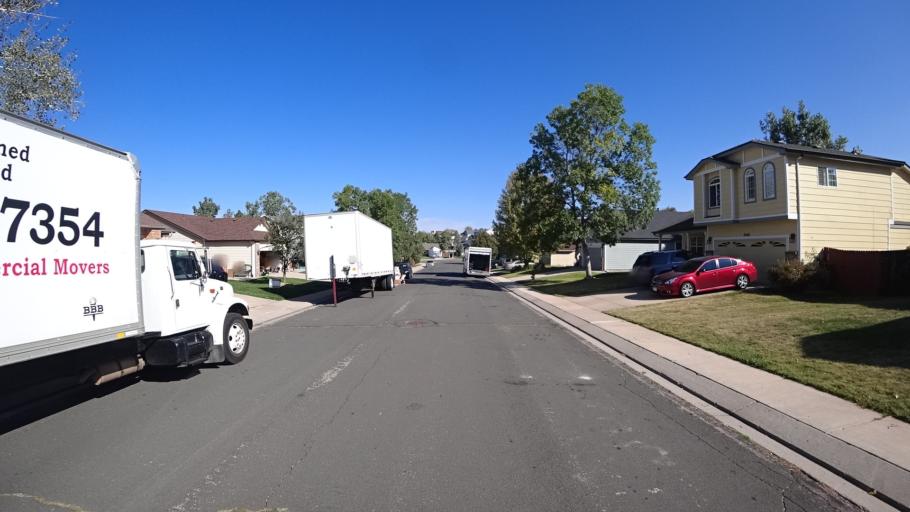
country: US
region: Colorado
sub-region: El Paso County
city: Cimarron Hills
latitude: 38.8786
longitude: -104.7041
